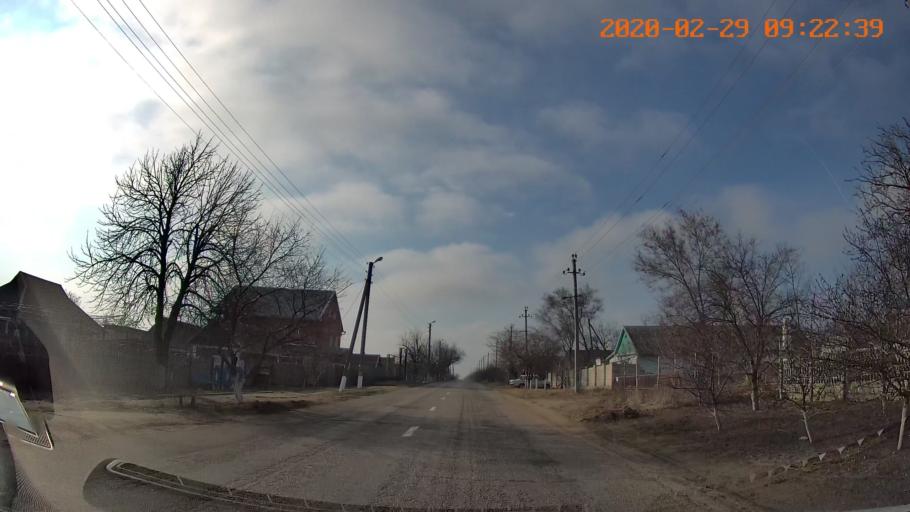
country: MD
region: Telenesti
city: Pervomaisc
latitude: 46.7334
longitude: 29.9635
